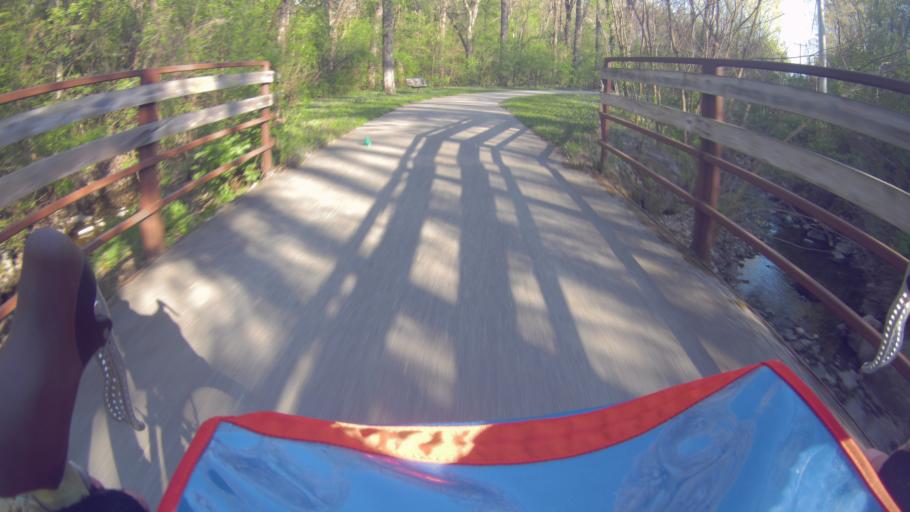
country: US
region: Wisconsin
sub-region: Dane County
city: Madison
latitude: 43.0186
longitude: -89.4260
